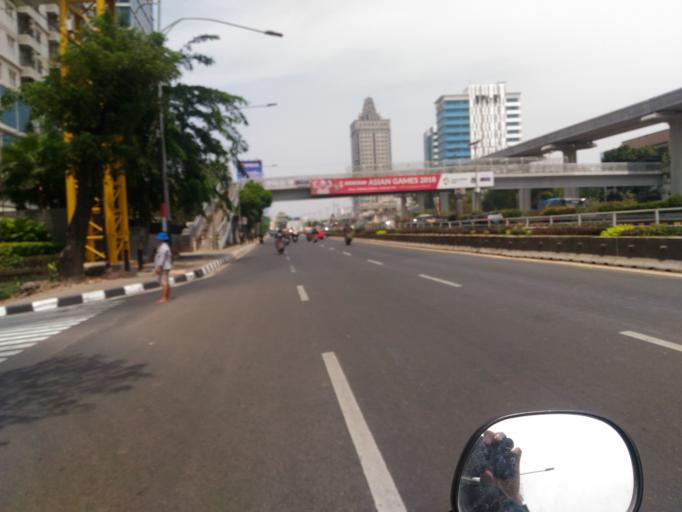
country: ID
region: Jakarta Raya
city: Jakarta
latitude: -6.2430
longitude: 106.8540
